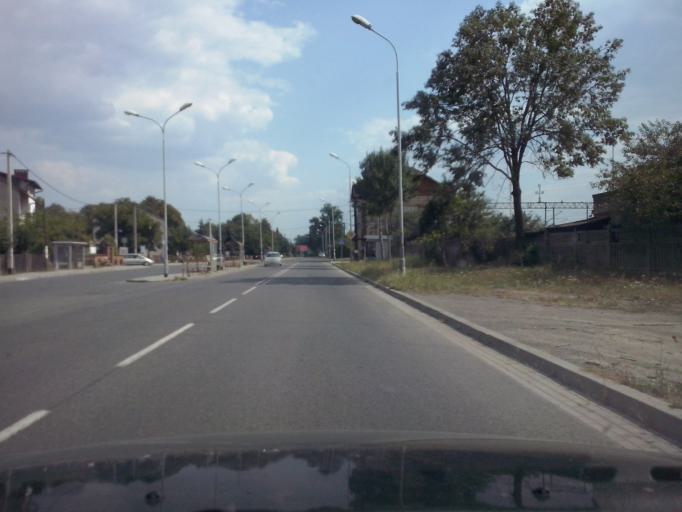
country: PL
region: Subcarpathian Voivodeship
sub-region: Powiat nizanski
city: Nisko
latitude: 50.5143
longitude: 22.1414
